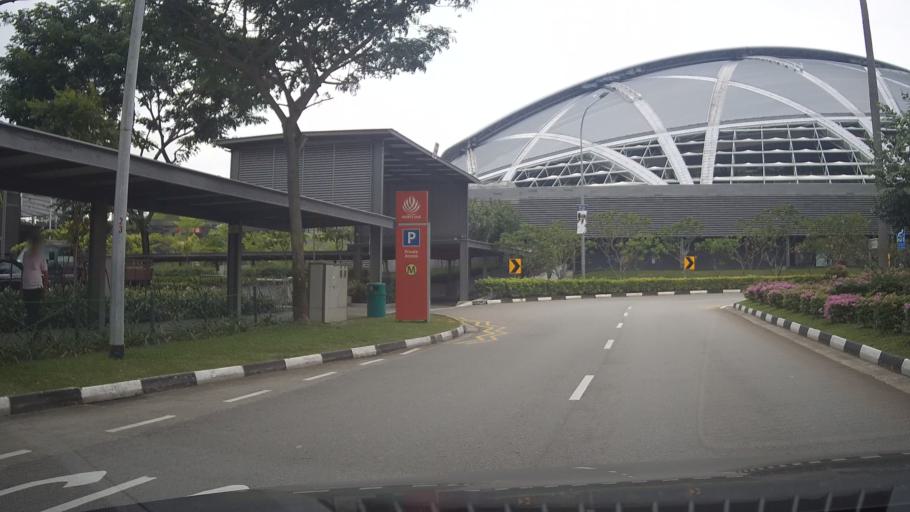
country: SG
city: Singapore
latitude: 1.3017
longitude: 103.8752
